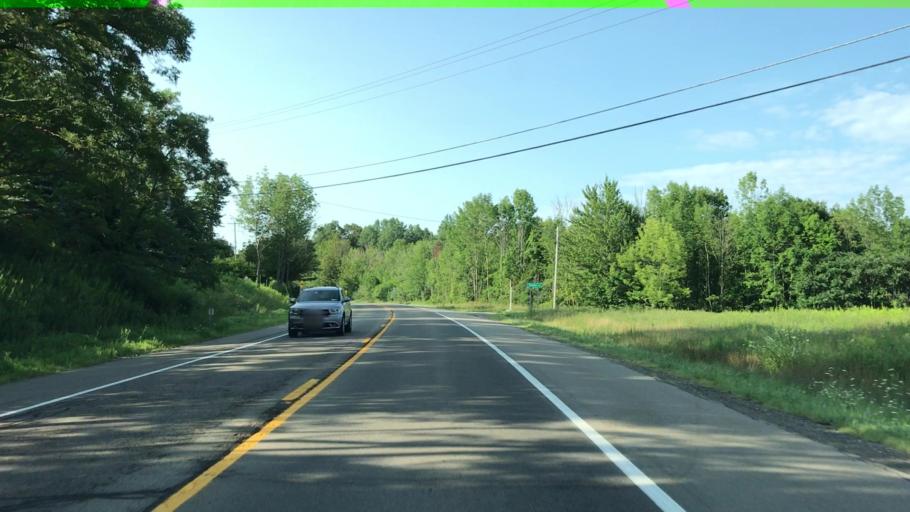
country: US
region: New York
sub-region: Chautauqua County
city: Fredonia
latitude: 42.3743
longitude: -79.3141
